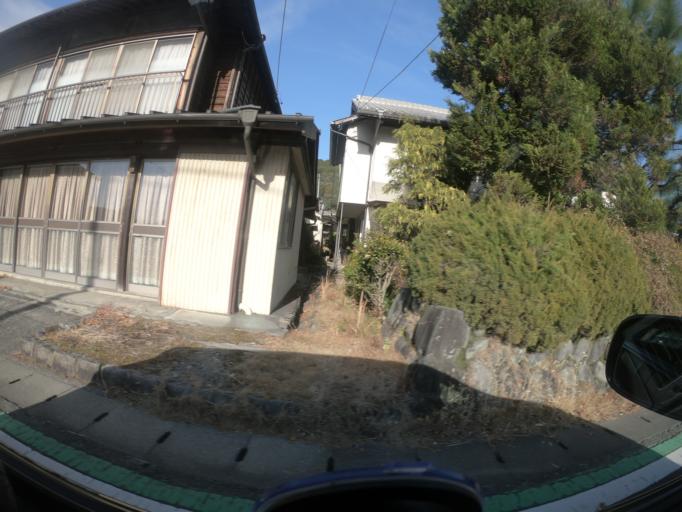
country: JP
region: Shizuoka
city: Kanaya
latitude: 35.0460
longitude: 138.0852
